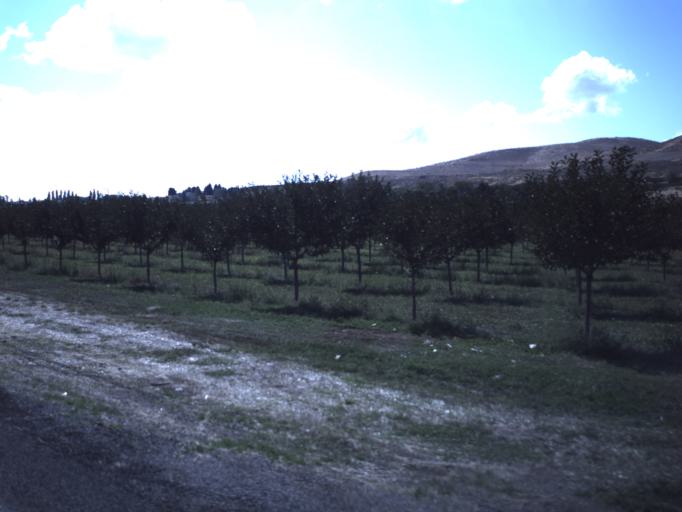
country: US
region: Utah
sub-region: Utah County
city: West Mountain
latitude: 40.0319
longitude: -111.7872
